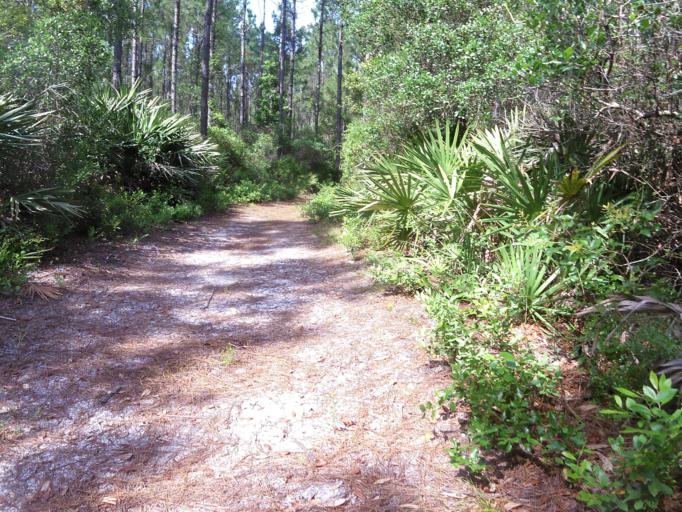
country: US
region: Florida
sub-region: Nassau County
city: Yulee
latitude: 30.4901
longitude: -81.4963
